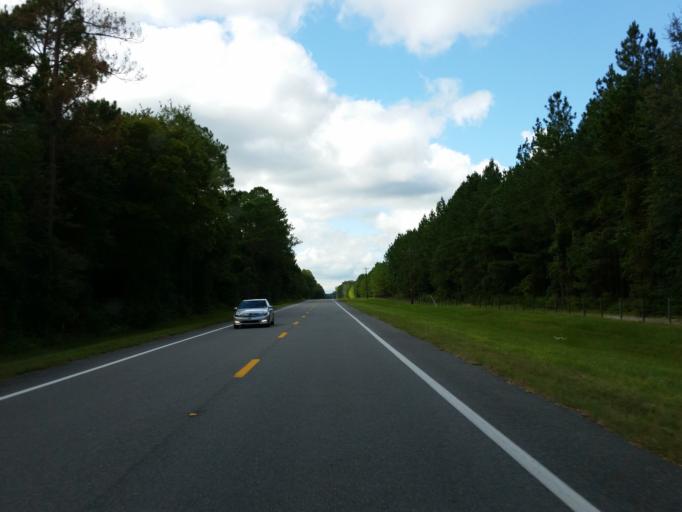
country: US
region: Florida
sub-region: Union County
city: Lake Butler
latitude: 30.0466
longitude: -82.3960
